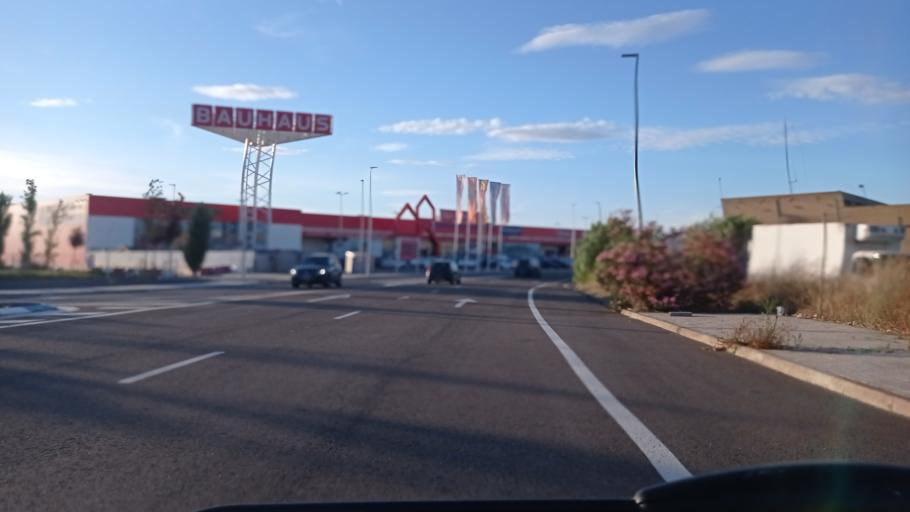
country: ES
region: Aragon
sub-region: Provincia de Zaragoza
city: Oliver-Valdefierro, Oliver, Valdefierro
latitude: 41.6736
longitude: -0.9504
